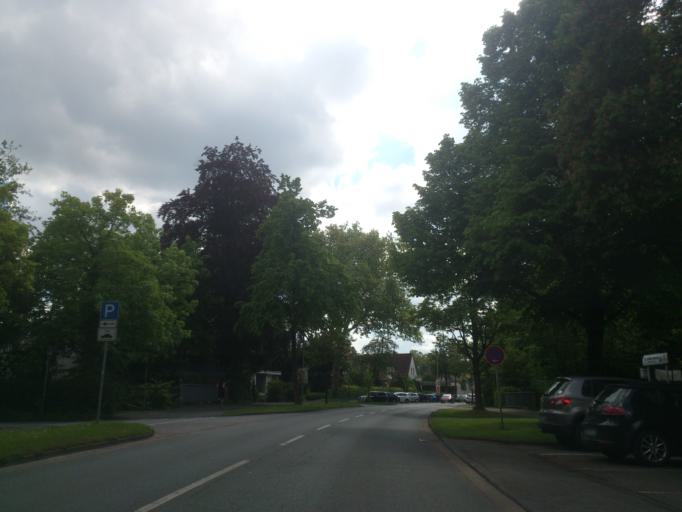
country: DE
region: North Rhine-Westphalia
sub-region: Regierungsbezirk Detmold
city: Paderborn
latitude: 51.7276
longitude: 8.7445
